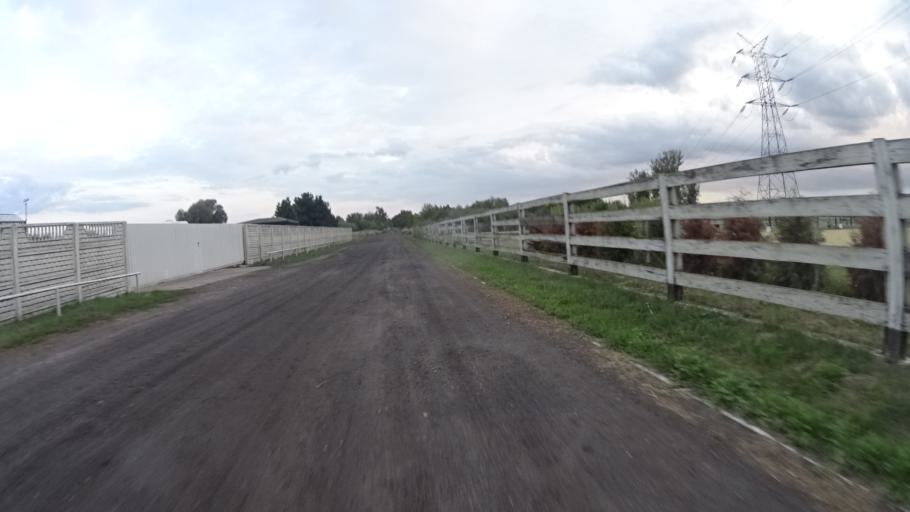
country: PL
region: Masovian Voivodeship
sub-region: Powiat warszawski zachodni
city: Ozarow Mazowiecki
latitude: 52.2357
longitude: 20.7657
